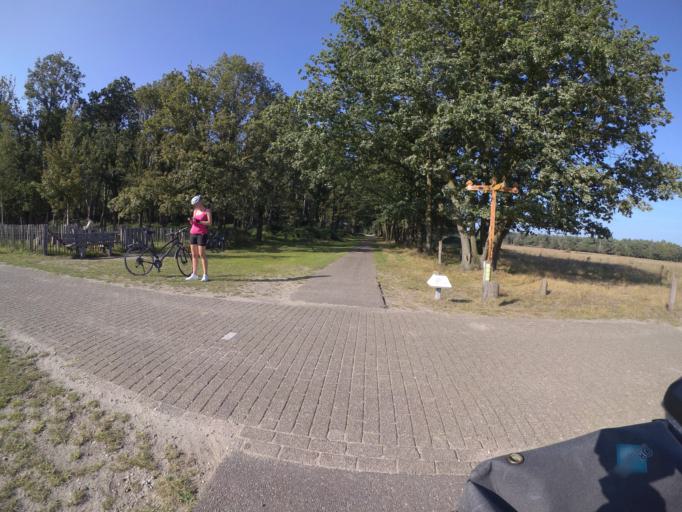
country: NL
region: North Brabant
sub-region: Gemeente Landerd
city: Schaijk
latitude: 51.7036
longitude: 5.6240
